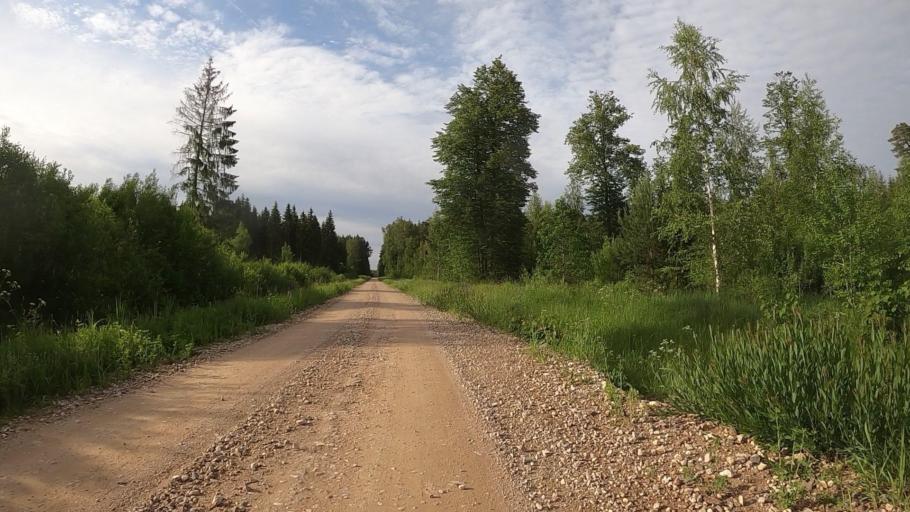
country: LV
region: Ozolnieku
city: Ozolnieki
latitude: 56.7564
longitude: 23.7919
